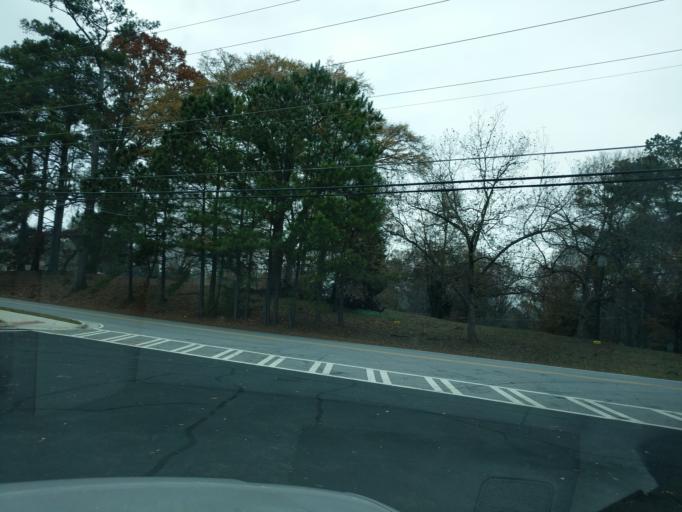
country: US
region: Georgia
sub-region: Gwinnett County
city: Duluth
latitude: 34.0072
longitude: -84.1525
